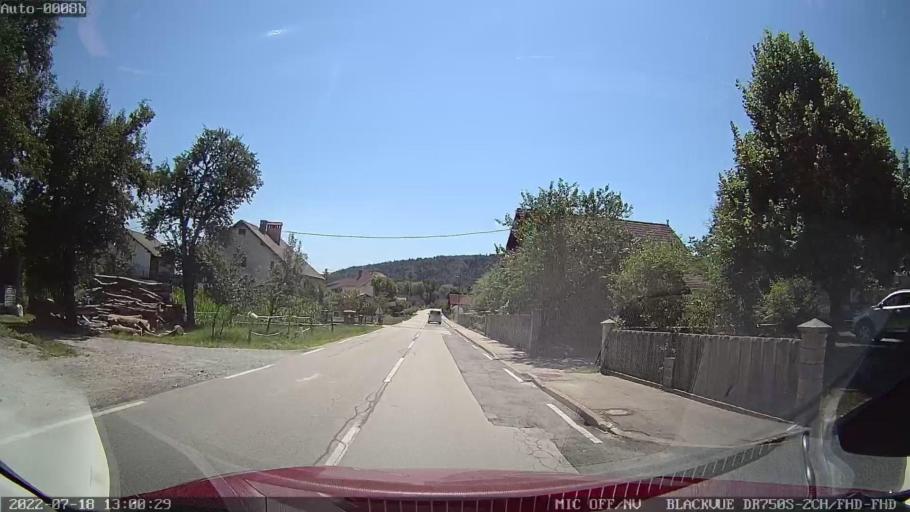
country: SI
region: Dobrova-Horjul-Polhov Gradec
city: Dobrova
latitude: 46.0625
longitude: 14.4127
